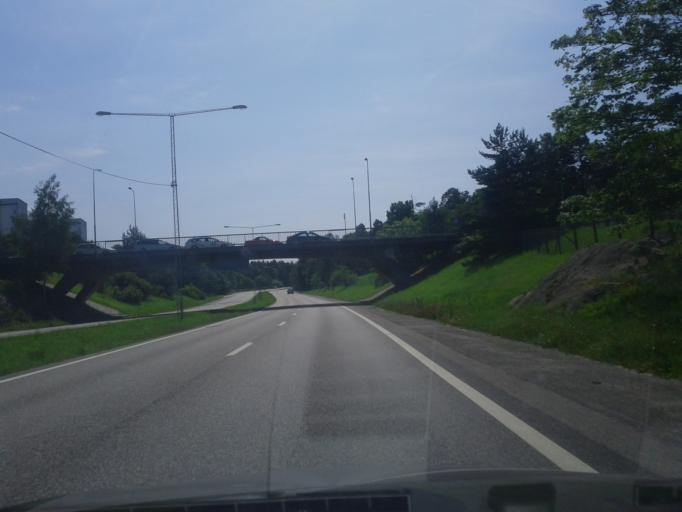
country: SE
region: Stockholm
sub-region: Huddinge Kommun
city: Huddinge
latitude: 59.2608
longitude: 18.0102
